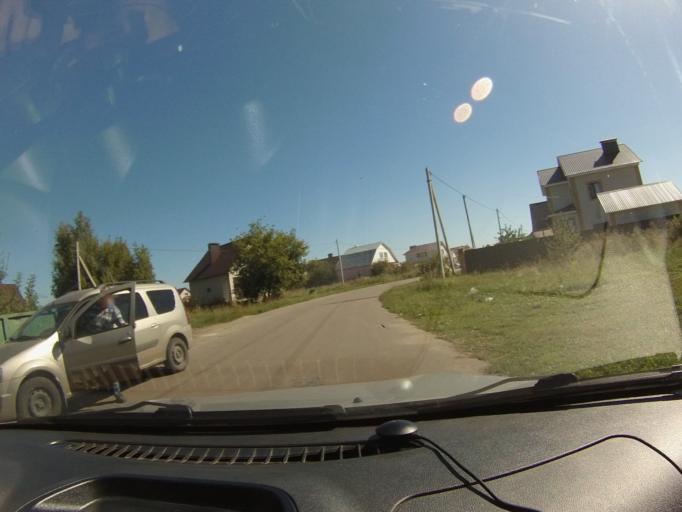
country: RU
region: Tambov
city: Komsomolets
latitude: 52.7661
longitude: 41.3625
